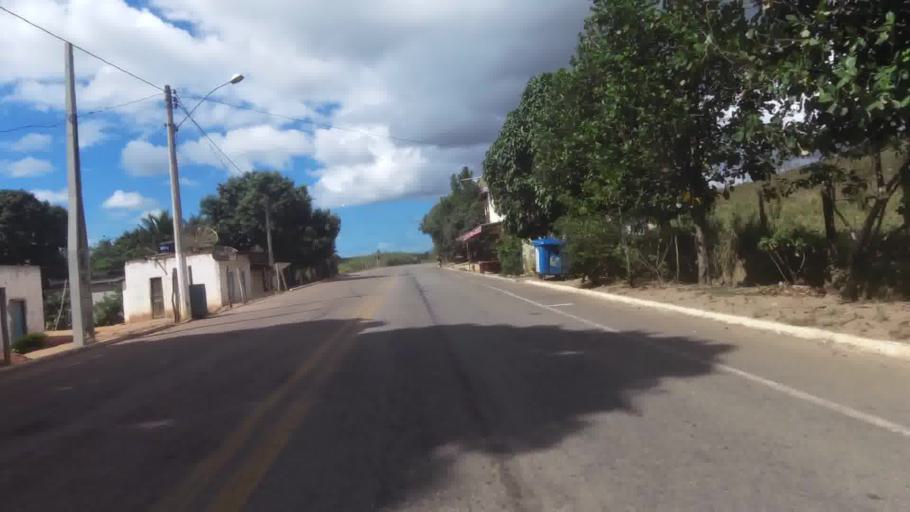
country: BR
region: Espirito Santo
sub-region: Marataizes
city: Marataizes
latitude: -21.1407
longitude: -41.0010
